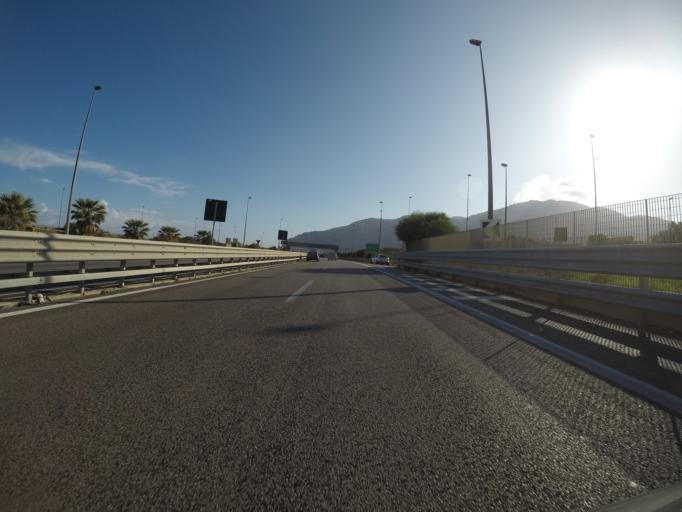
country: IT
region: Sicily
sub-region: Palermo
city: Capaci
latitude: 38.1746
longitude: 13.2160
